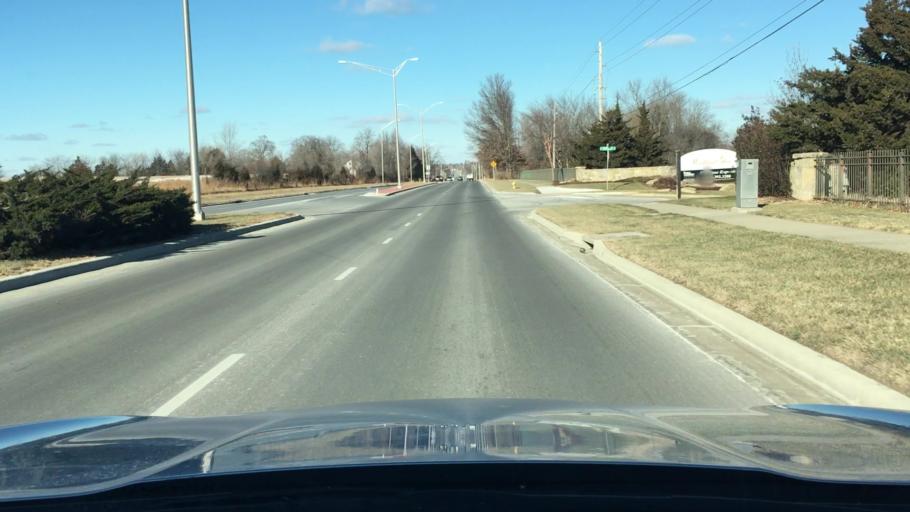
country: US
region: Missouri
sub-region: Jackson County
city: Lees Summit
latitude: 38.8918
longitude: -94.3963
